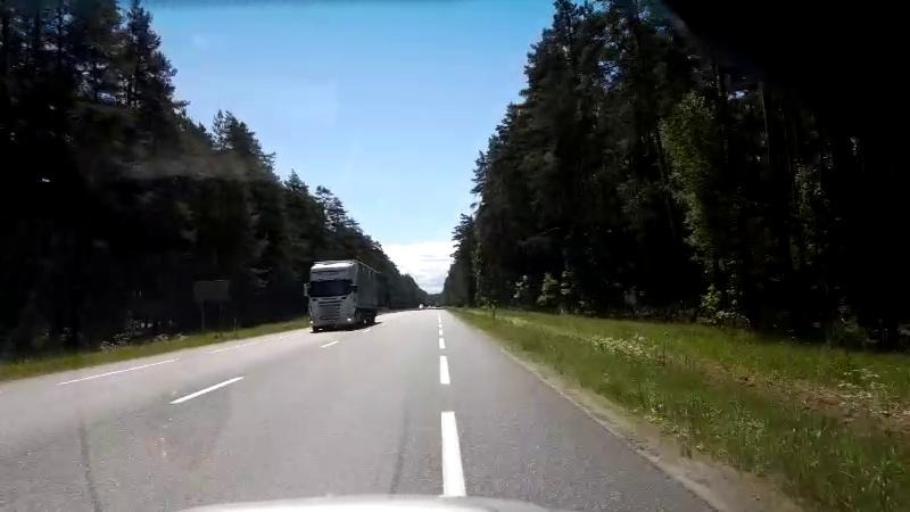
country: LV
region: Saulkrastu
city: Saulkrasti
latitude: 57.3615
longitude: 24.4374
